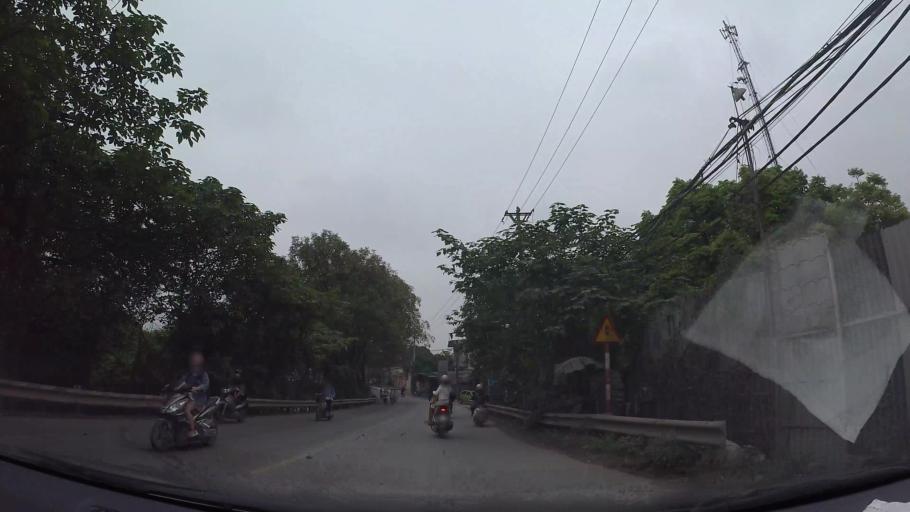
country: VN
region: Hung Yen
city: Van Giang
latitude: 20.9789
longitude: 105.8909
